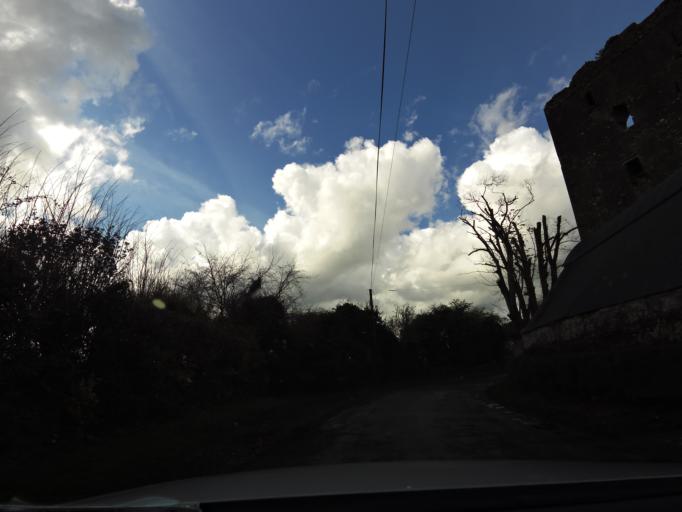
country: IE
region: Leinster
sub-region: Laois
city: Rathdowney
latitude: 52.8158
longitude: -7.4729
